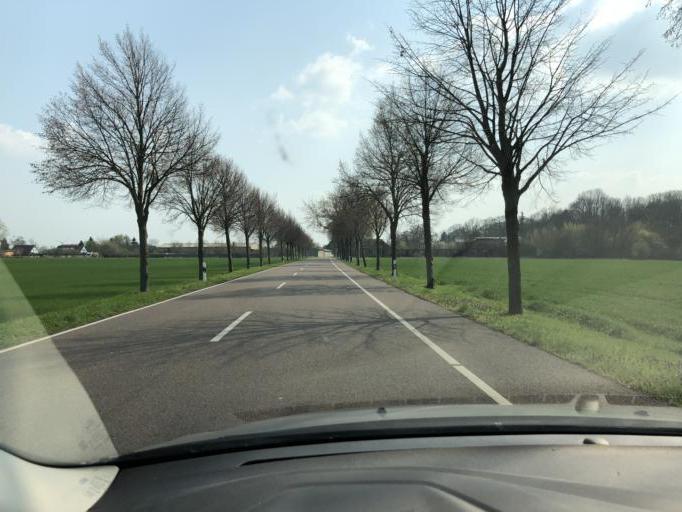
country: DE
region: Saxony-Anhalt
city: Niemberg
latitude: 51.5955
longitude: 12.0695
